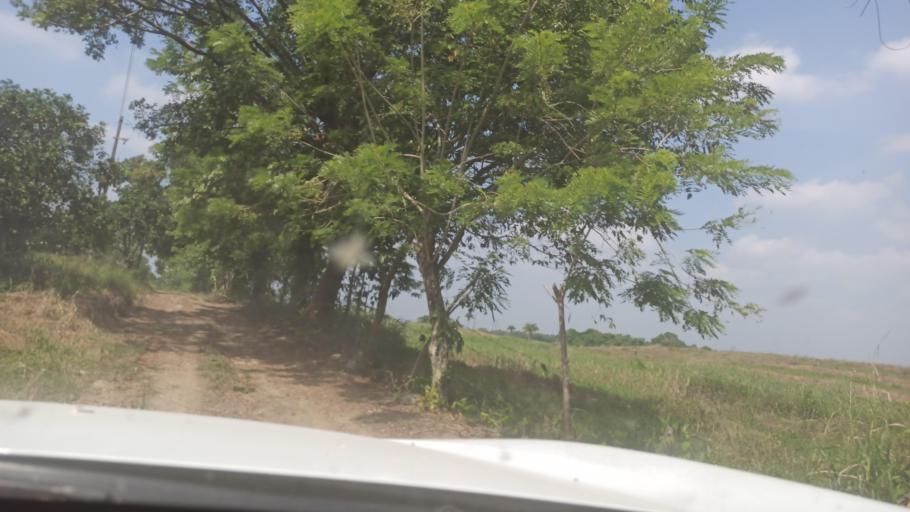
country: MX
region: Veracruz
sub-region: Atzalan
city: Colonias Pedernales
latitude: 20.0398
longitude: -97.0069
